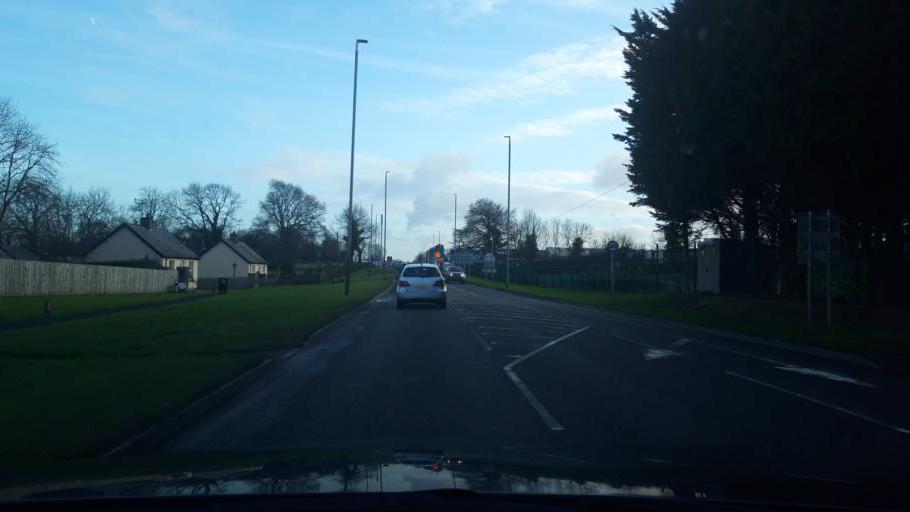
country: GB
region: Northern Ireland
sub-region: Dungannon District
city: Dungannon
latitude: 54.4882
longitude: -6.7466
